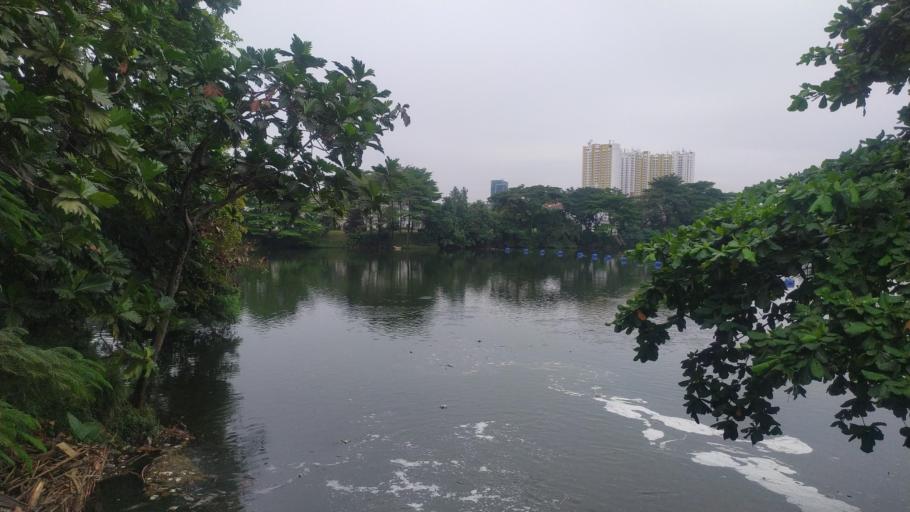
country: ID
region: Banten
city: Tangerang
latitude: -6.2268
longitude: 106.6268
